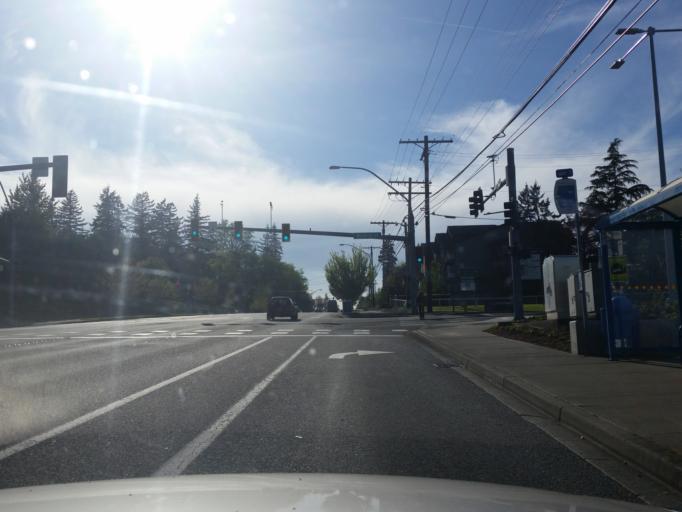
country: US
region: Washington
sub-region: Snohomish County
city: Alderwood Manor
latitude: 47.8501
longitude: -122.2762
